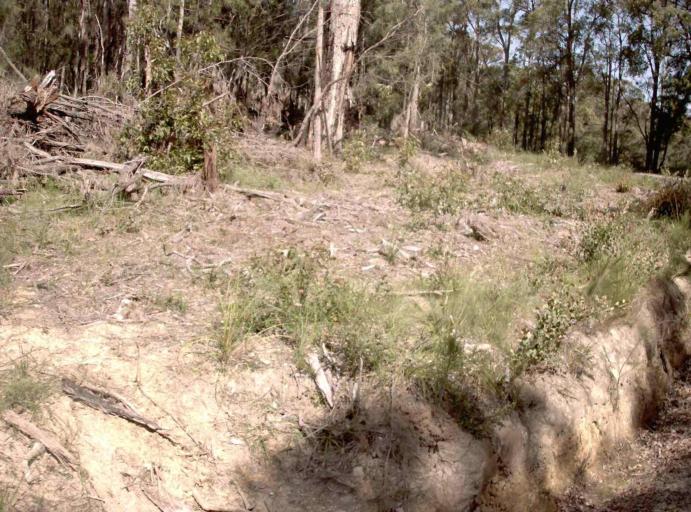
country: AU
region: New South Wales
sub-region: Bega Valley
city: Eden
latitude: -37.5328
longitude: 149.6947
